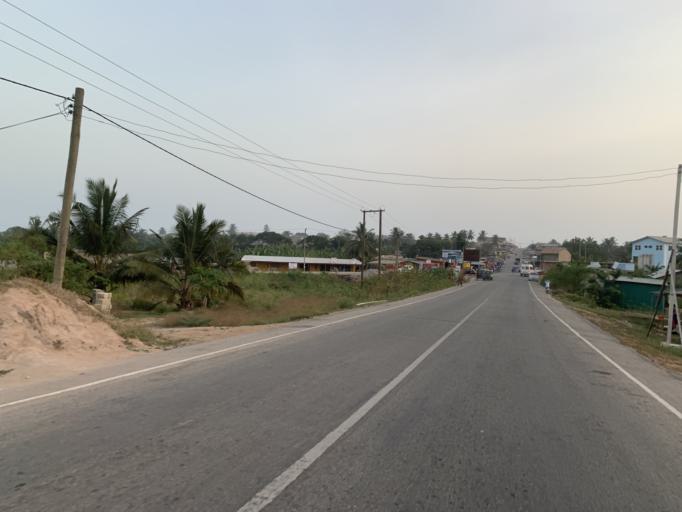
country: GH
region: Central
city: Winneba
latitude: 5.3578
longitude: -0.6102
